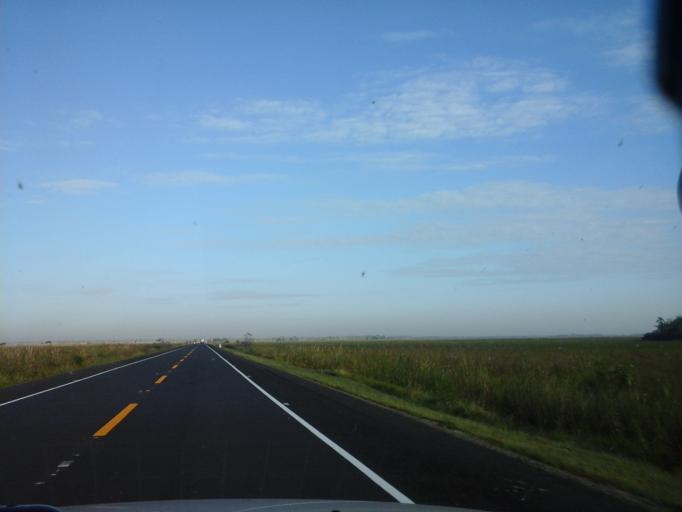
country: PY
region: Neembucu
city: Cerrito
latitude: -26.8936
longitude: -57.7022
